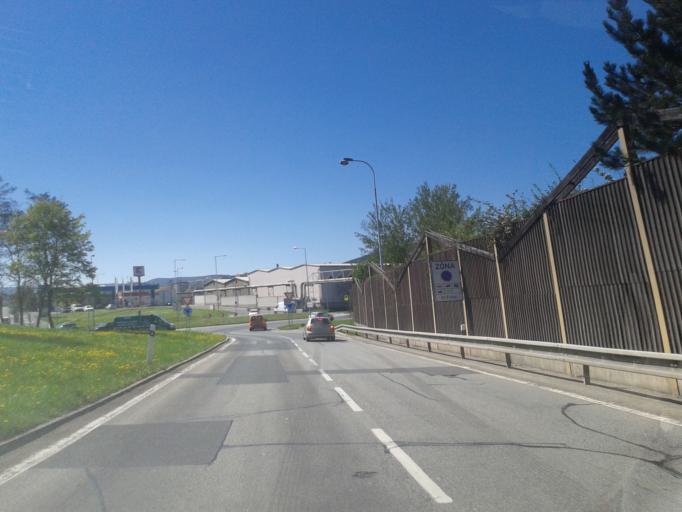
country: CZ
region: Central Bohemia
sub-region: Okres Beroun
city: Beroun
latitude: 49.9573
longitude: 14.0652
